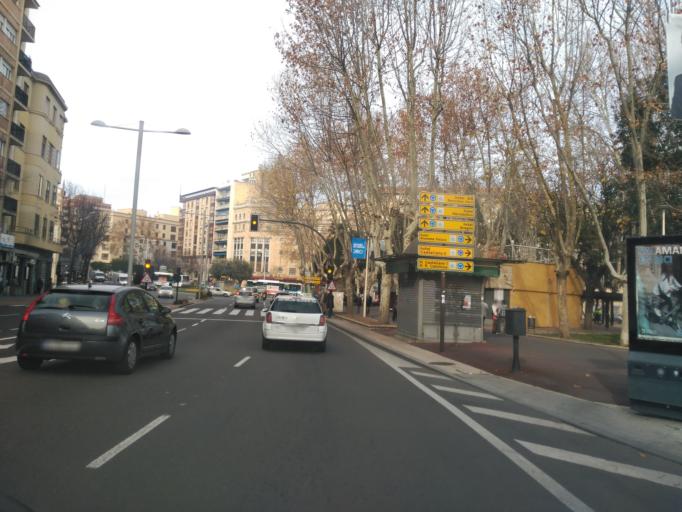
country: ES
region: Castille and Leon
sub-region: Provincia de Salamanca
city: Salamanca
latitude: 40.9676
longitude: -5.6581
